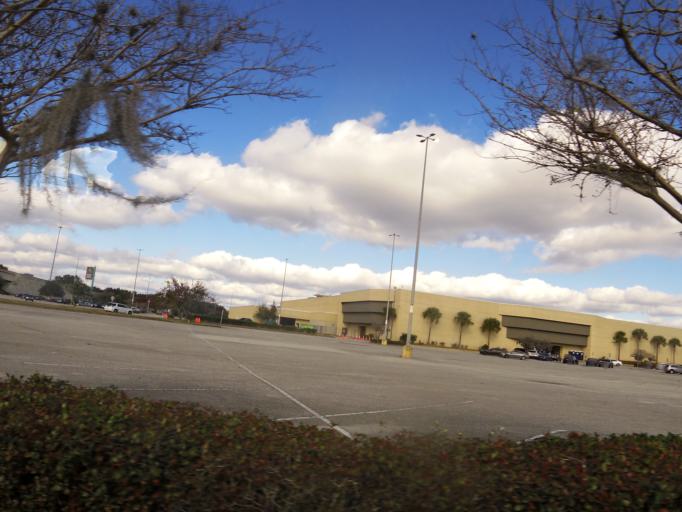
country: US
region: Florida
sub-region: Duval County
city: Jacksonville
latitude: 30.3228
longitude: -81.5571
